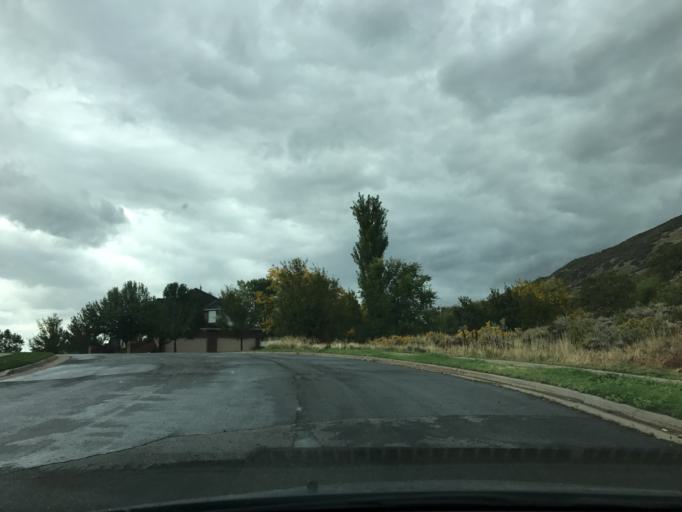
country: US
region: Utah
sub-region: Davis County
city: Fruit Heights
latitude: 41.0207
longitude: -111.8992
